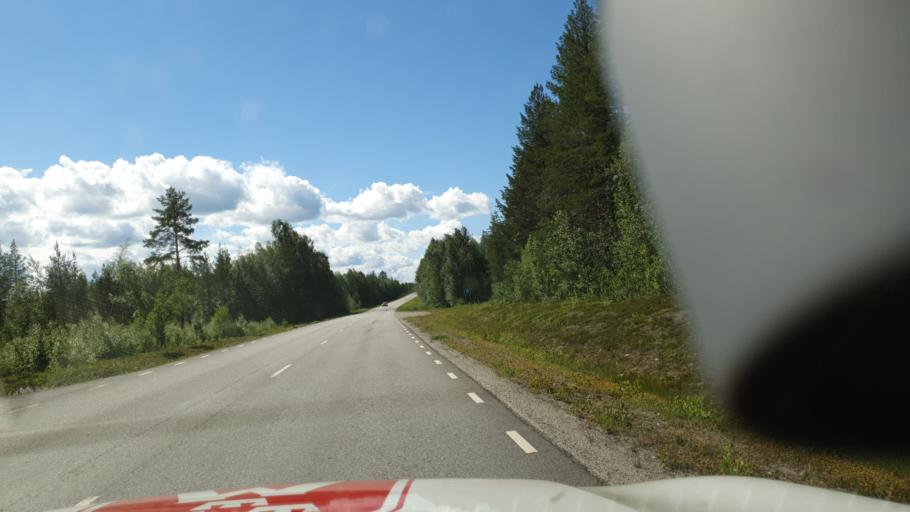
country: SE
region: Vaesterbotten
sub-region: Lycksele Kommun
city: Lycksele
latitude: 64.6838
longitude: 18.6983
